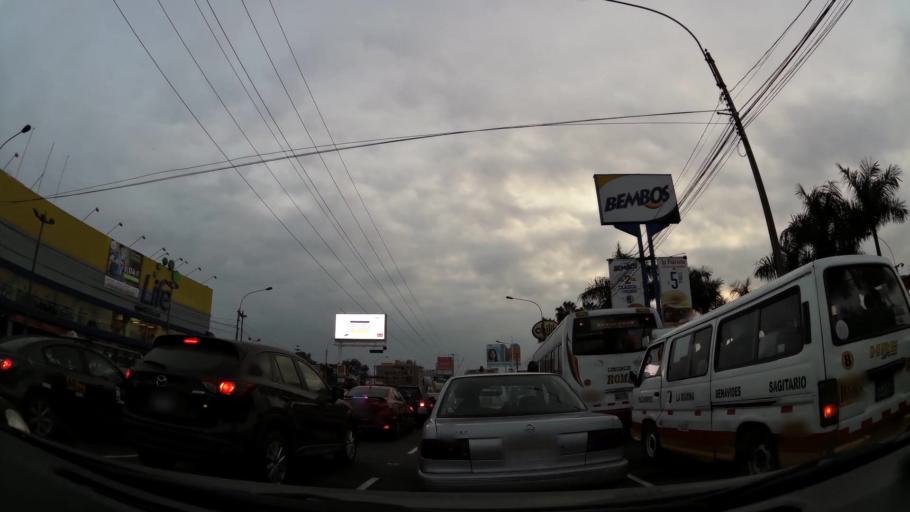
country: PE
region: Callao
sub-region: Callao
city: Callao
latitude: -12.0781
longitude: -77.0835
